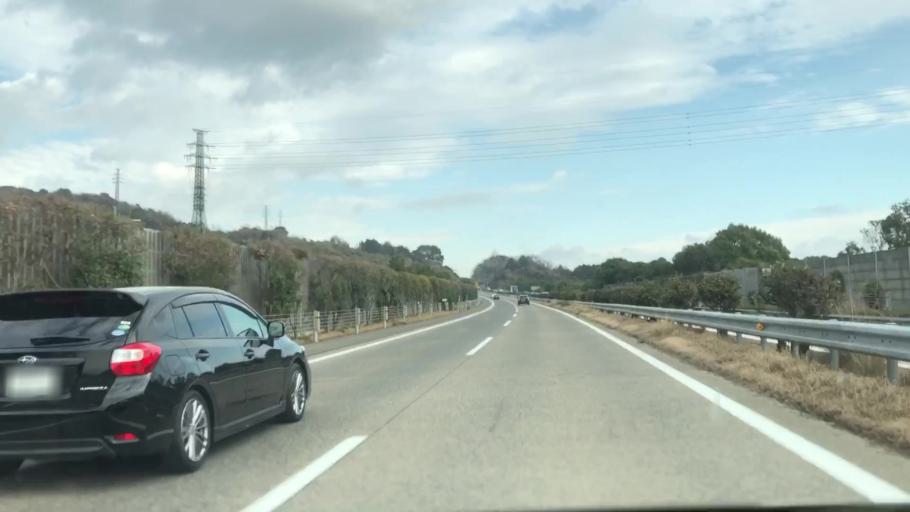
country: JP
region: Saga Prefecture
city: Kanzakimachi-kanzaki
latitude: 33.3547
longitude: 130.4153
